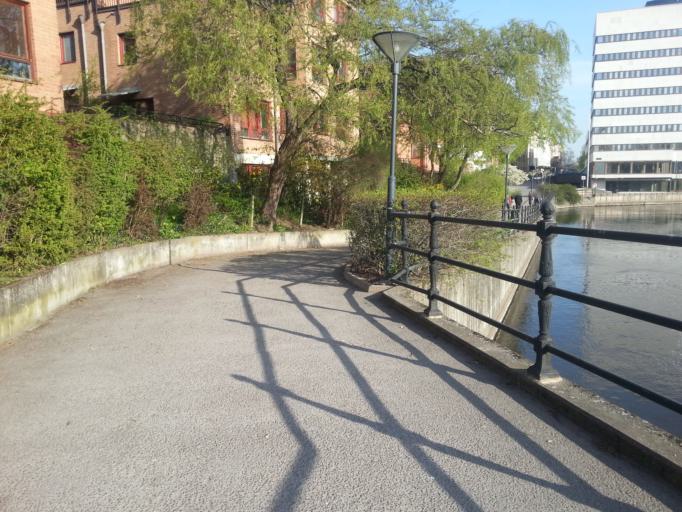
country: SE
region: OEstergoetland
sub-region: Norrkopings Kommun
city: Norrkoping
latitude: 58.5920
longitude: 16.1827
